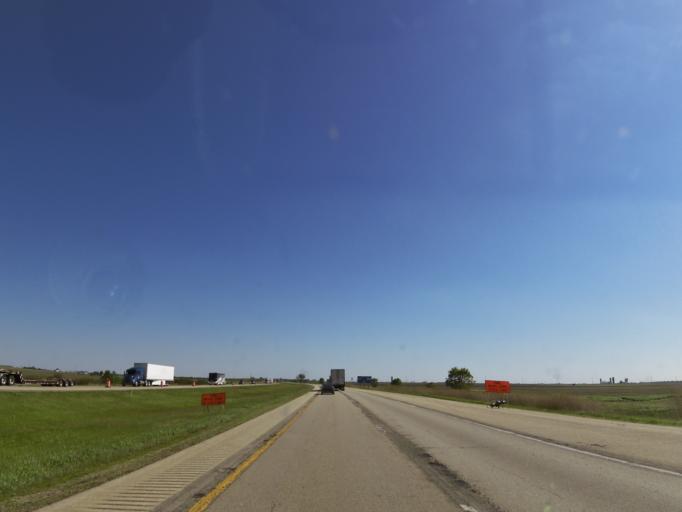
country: US
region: Illinois
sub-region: Ogle County
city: Hillcrest
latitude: 41.9621
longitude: -89.0243
